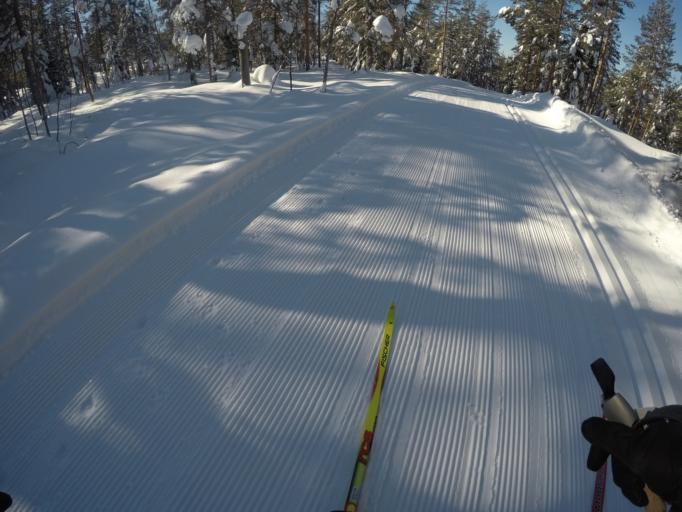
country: SE
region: Vaesternorrland
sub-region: Sundsvalls Kommun
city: Sundsvall
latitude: 62.3665
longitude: 17.3025
